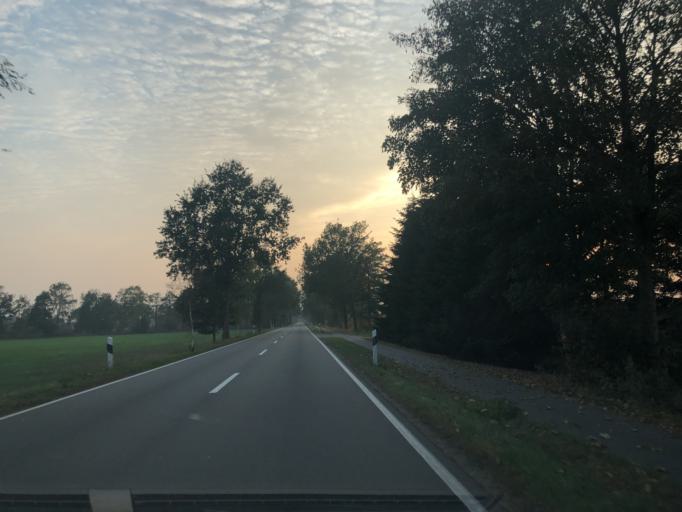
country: DE
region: Lower Saxony
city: Garrel
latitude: 53.0179
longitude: 8.0545
